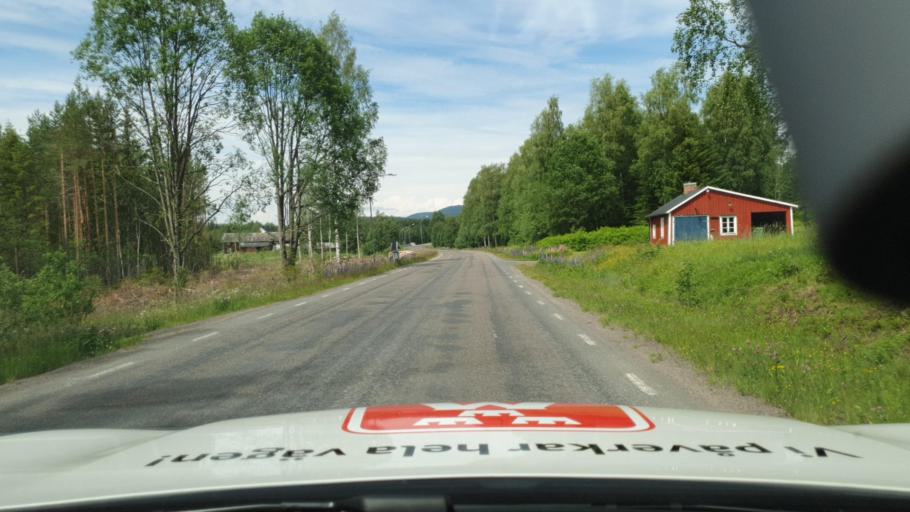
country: NO
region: Hedmark
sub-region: Grue
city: Kirkenaer
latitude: 60.7003
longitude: 12.6163
